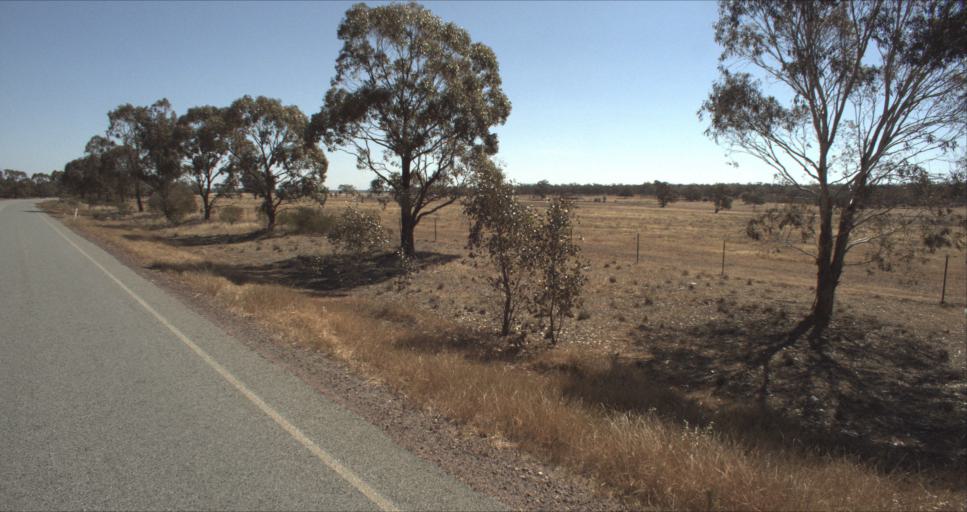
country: AU
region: New South Wales
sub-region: Leeton
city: Leeton
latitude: -34.4854
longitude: 146.4732
